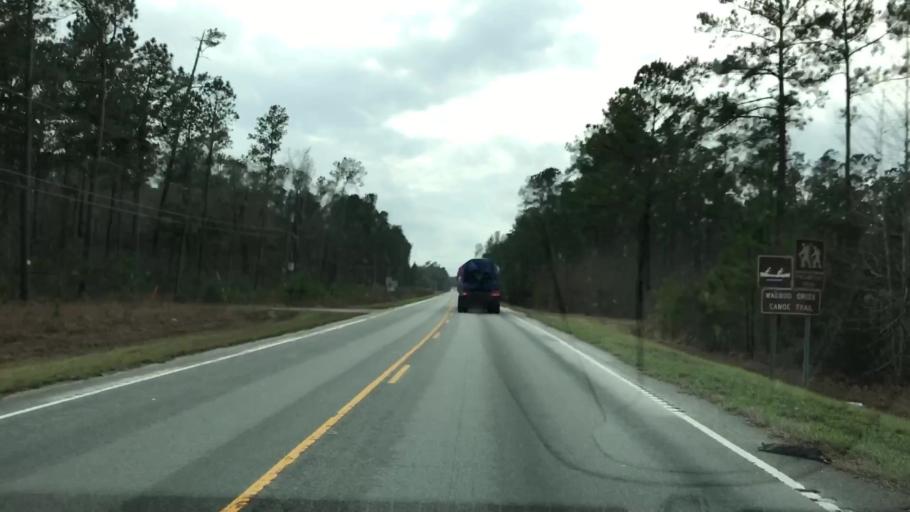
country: US
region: South Carolina
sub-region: Berkeley County
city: Bonneau Beach
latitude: 33.2637
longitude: -79.9233
